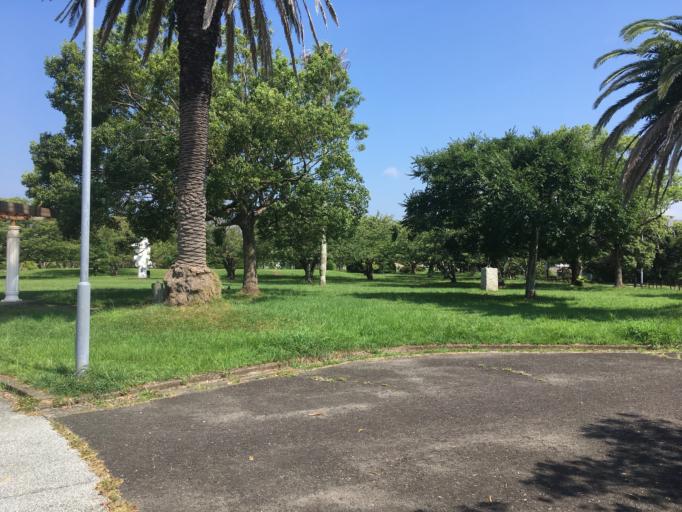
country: JP
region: Chiba
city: Tateyama
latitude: 34.9939
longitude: 139.8674
